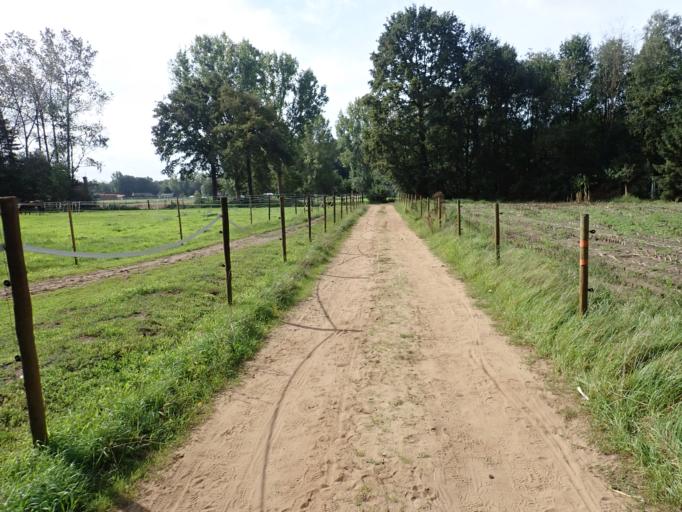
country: BE
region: Flanders
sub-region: Provincie Antwerpen
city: Lille
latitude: 51.2362
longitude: 4.8139
